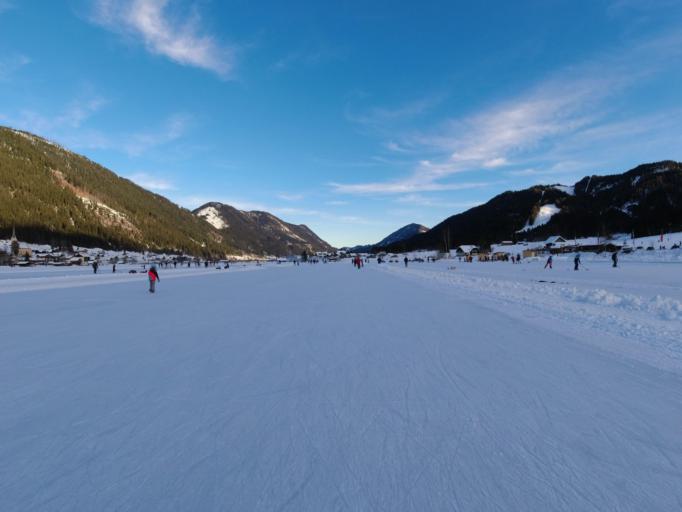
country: AT
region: Carinthia
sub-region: Politischer Bezirk Spittal an der Drau
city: Steinfeld
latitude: 46.7146
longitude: 13.2836
